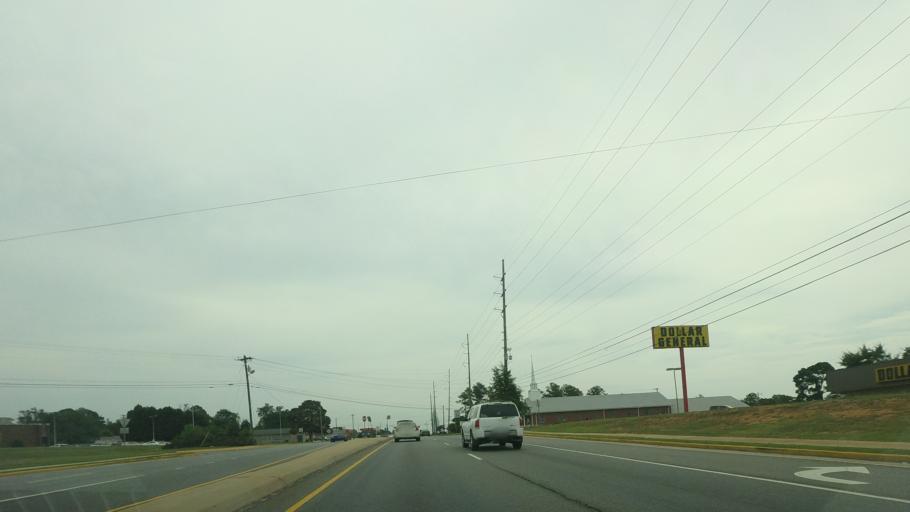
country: US
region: Georgia
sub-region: Houston County
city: Centerville
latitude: 32.5938
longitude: -83.6545
